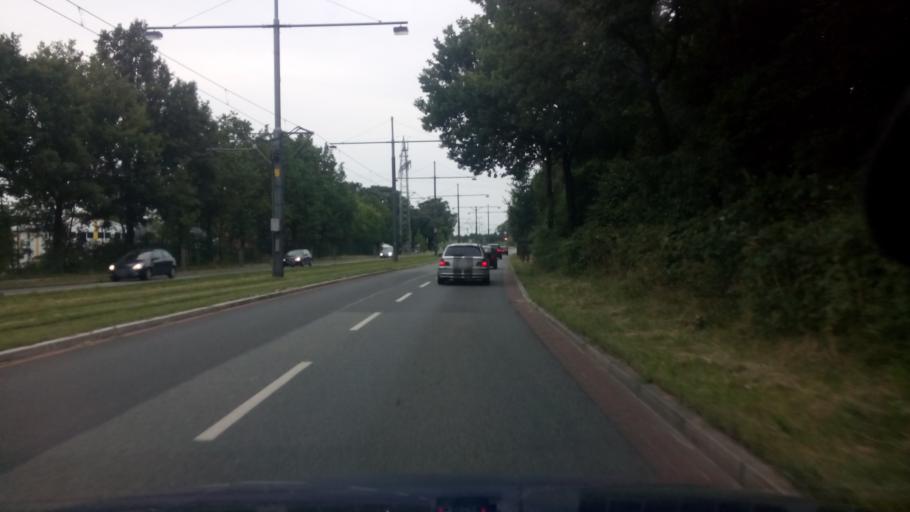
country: DE
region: Lower Saxony
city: Lilienthal
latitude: 53.1279
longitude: 8.8989
